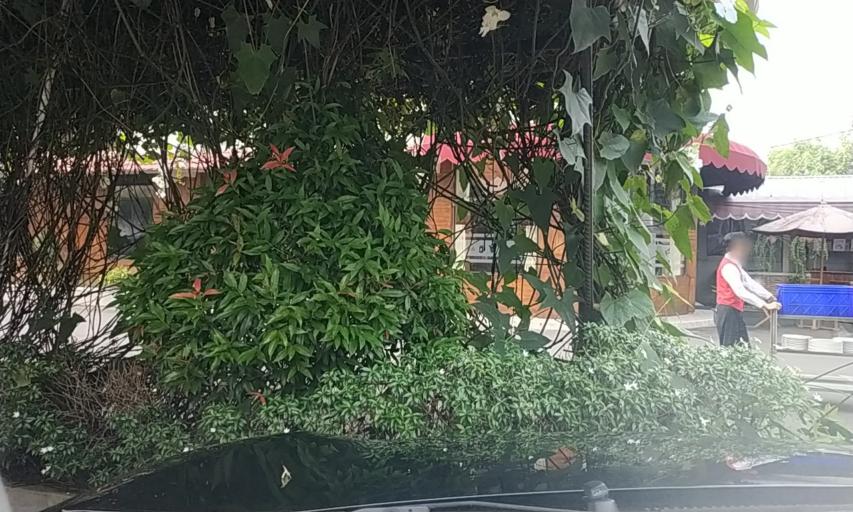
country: ID
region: Central Java
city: Purwokerto
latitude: -7.4181
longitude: 109.2544
